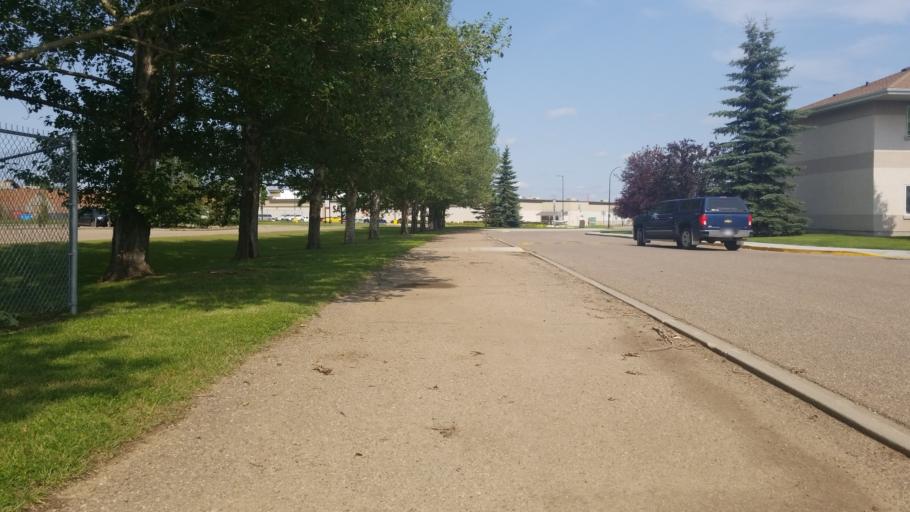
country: CA
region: Saskatchewan
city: Lloydminster
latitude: 53.2756
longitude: -110.0169
